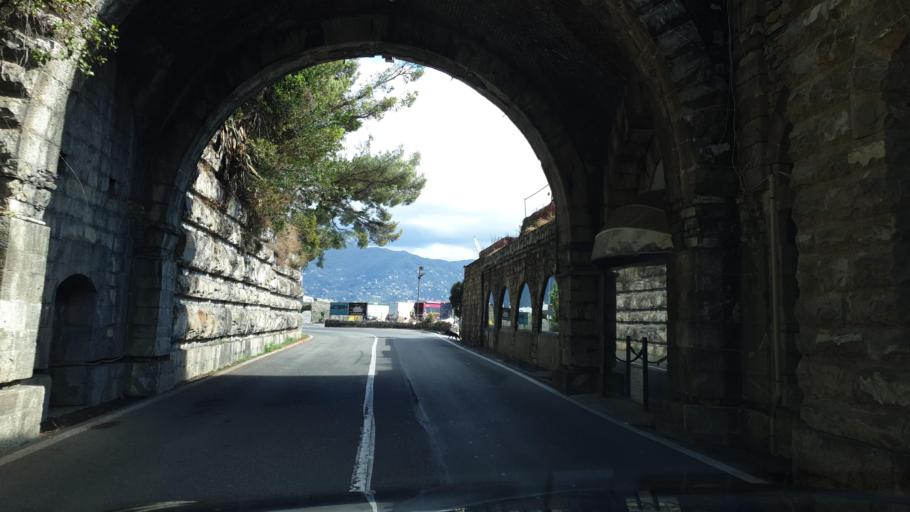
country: IT
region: Liguria
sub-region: Provincia di Genova
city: Santa Margherita Ligure
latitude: 44.3214
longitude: 9.2150
